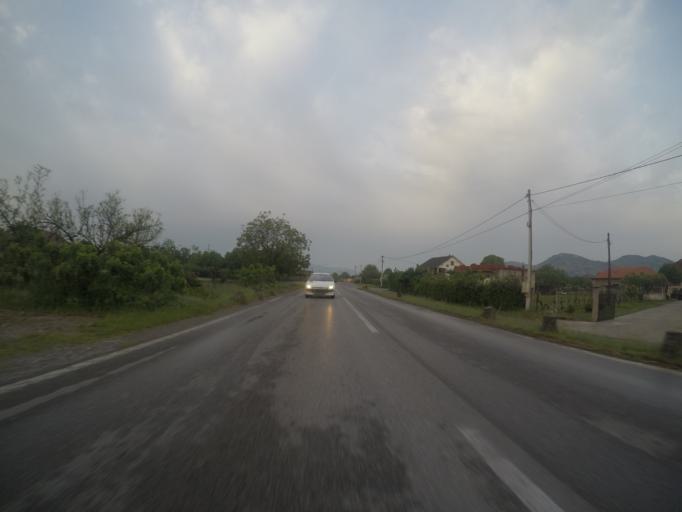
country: ME
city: Golubovci
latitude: 42.3258
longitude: 19.2189
